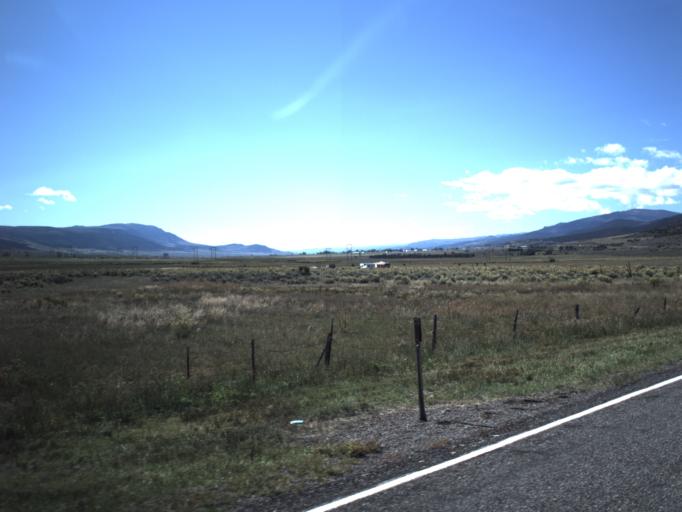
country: US
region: Utah
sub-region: Wayne County
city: Loa
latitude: 38.5612
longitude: -111.8545
